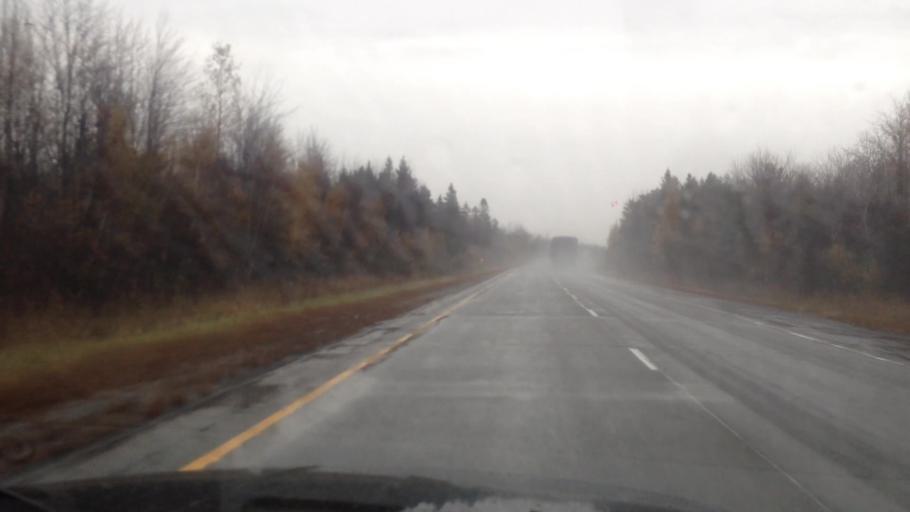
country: CA
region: Ontario
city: Casselman
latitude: 45.3139
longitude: -75.1992
